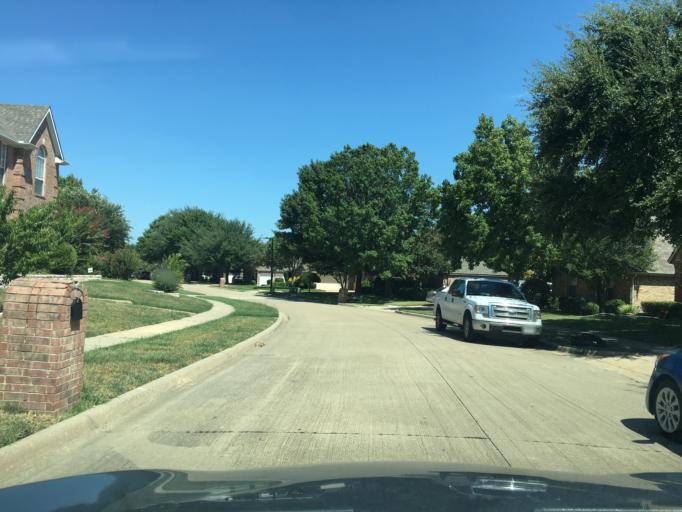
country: US
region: Texas
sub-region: Dallas County
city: Sachse
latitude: 32.9621
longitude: -96.6276
